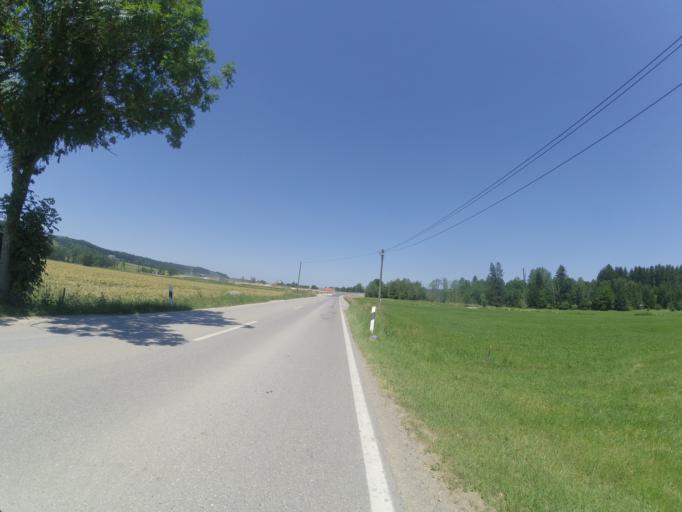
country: DE
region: Bavaria
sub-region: Swabia
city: Ottobeuren
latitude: 47.9179
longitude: 10.3093
